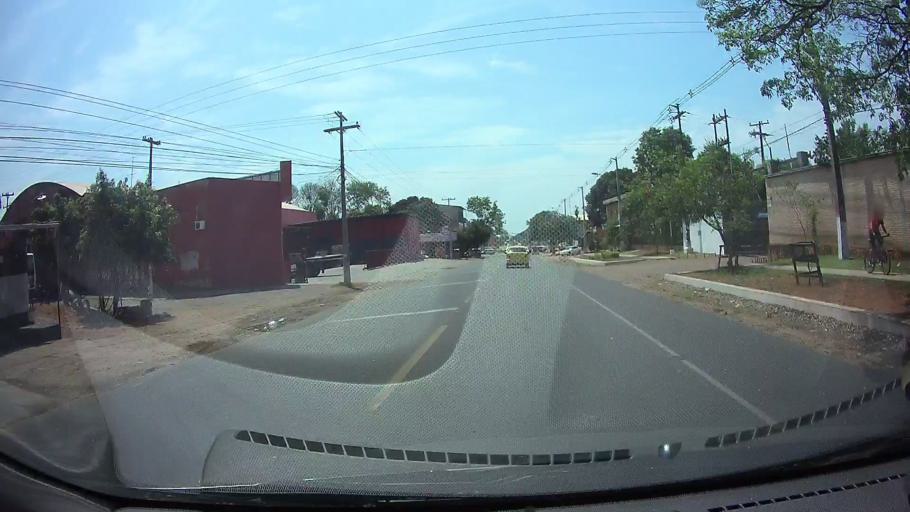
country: PY
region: Central
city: Capiata
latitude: -25.3749
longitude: -57.4772
